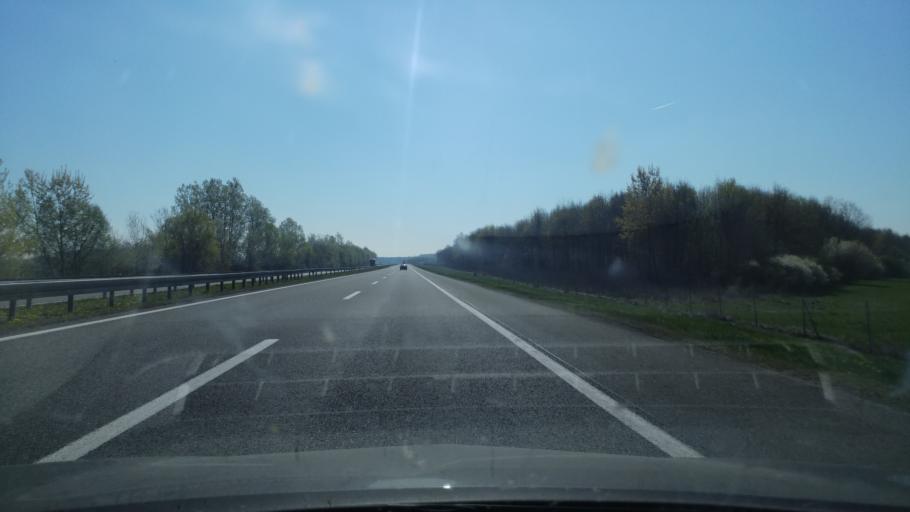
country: HR
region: Brodsko-Posavska
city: Garcin
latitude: 45.1660
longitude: 18.1704
